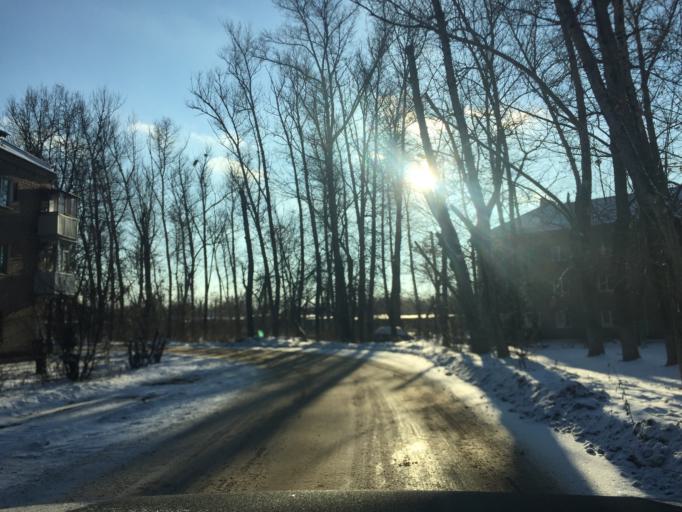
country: RU
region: Tula
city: Tula
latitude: 54.1802
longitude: 37.7016
